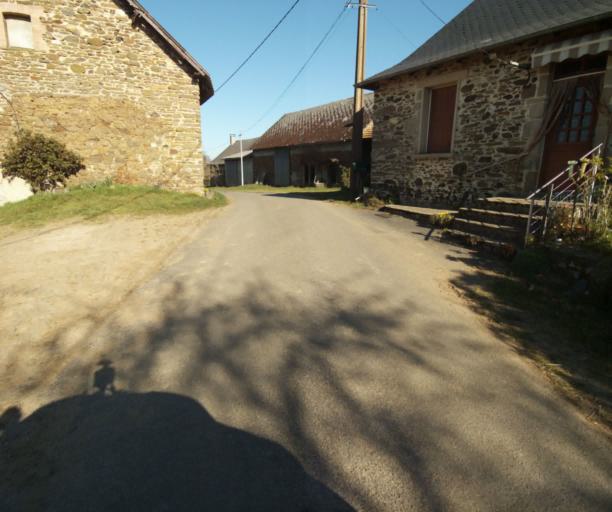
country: FR
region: Limousin
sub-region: Departement de la Correze
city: Saint-Clement
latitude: 45.3753
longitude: 1.6564
